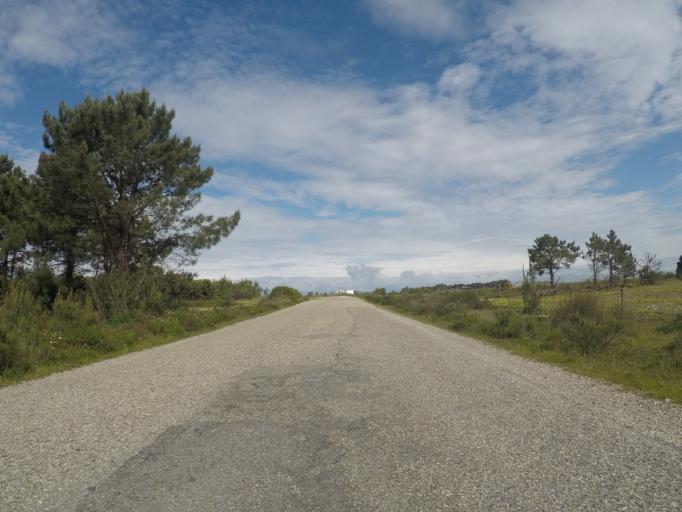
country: PT
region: Beja
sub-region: Odemira
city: Sao Teotonio
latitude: 37.4488
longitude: -8.7649
